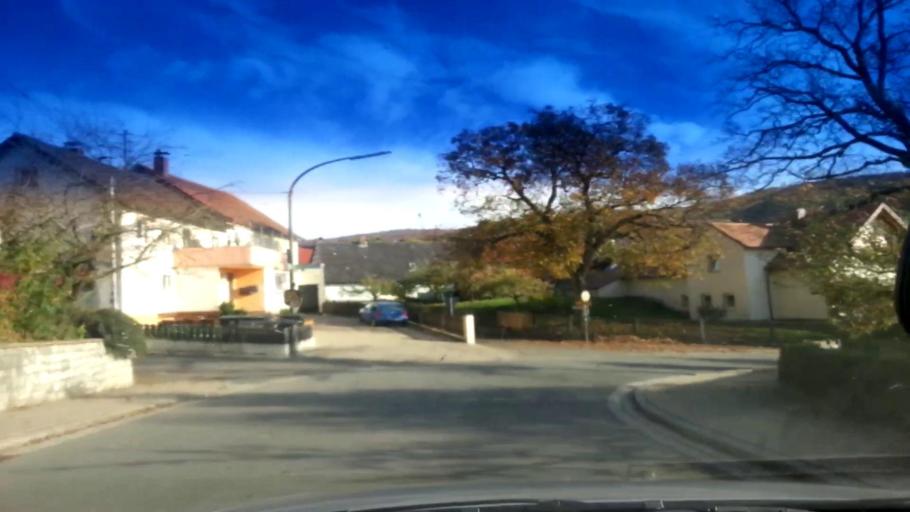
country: DE
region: Bavaria
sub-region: Upper Franconia
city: Litzendorf
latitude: 49.9005
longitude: 11.0328
